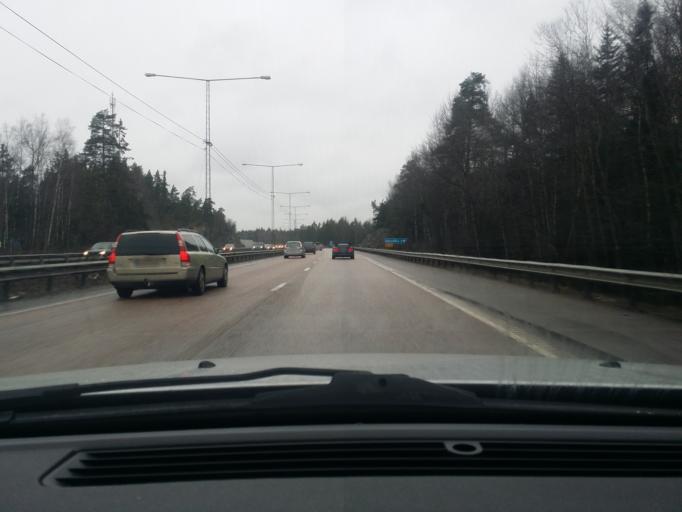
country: SE
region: Stockholm
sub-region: Jarfalla Kommun
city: Jakobsberg
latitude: 59.4450
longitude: 17.8414
